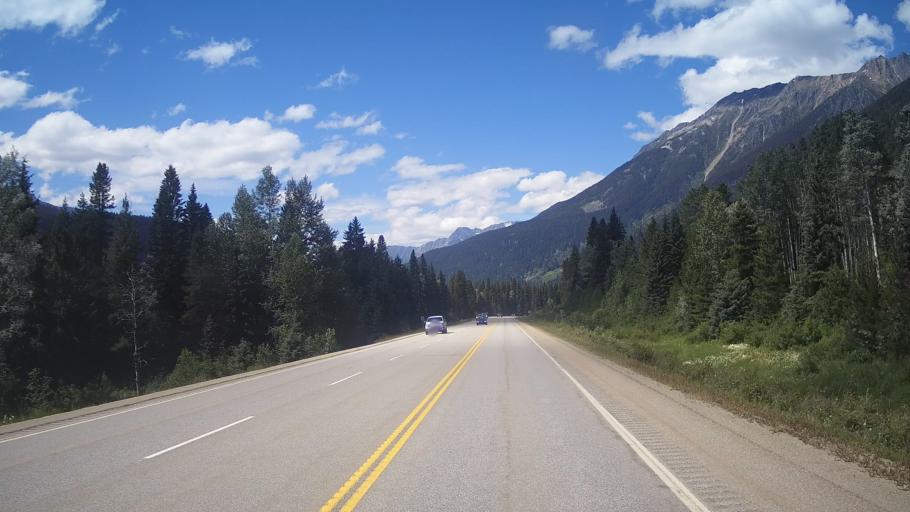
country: CA
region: Alberta
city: Grande Cache
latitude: 53.0078
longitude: -119.0586
